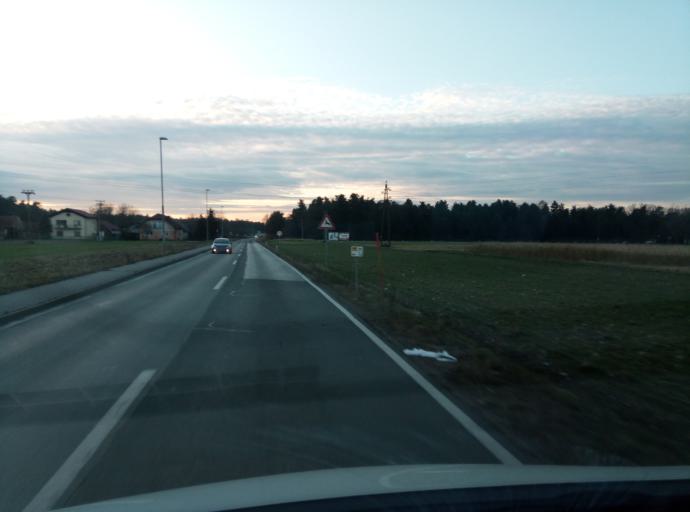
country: SI
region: Hajdina
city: Spodnja Hajdina
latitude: 46.4129
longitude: 15.8205
